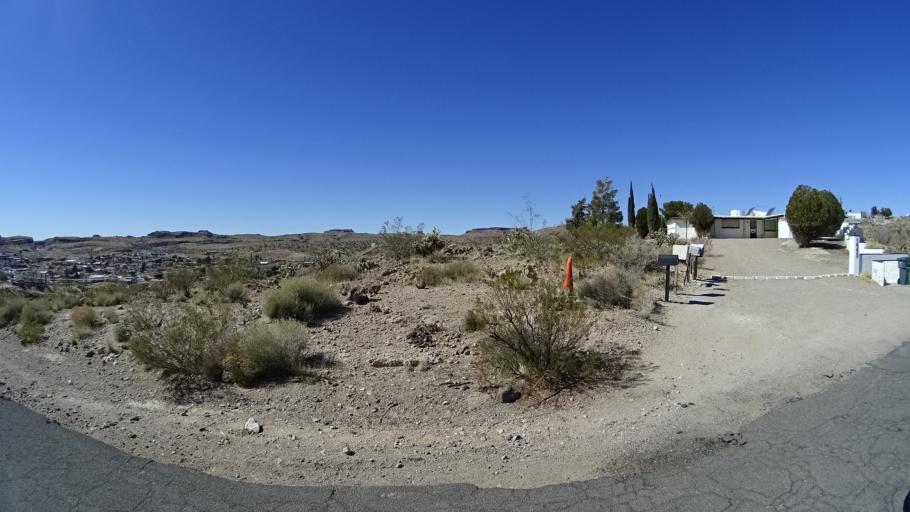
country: US
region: Arizona
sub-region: Mohave County
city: Kingman
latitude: 35.1992
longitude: -114.0567
